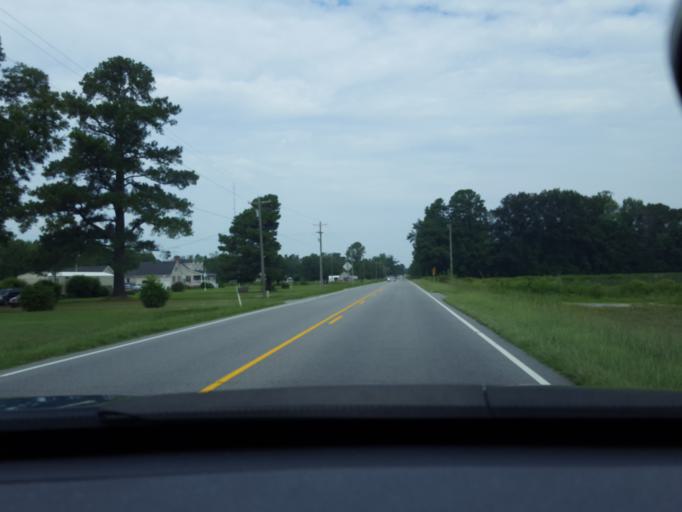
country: US
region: North Carolina
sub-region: Chowan County
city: Edenton
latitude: 36.1239
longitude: -76.6498
